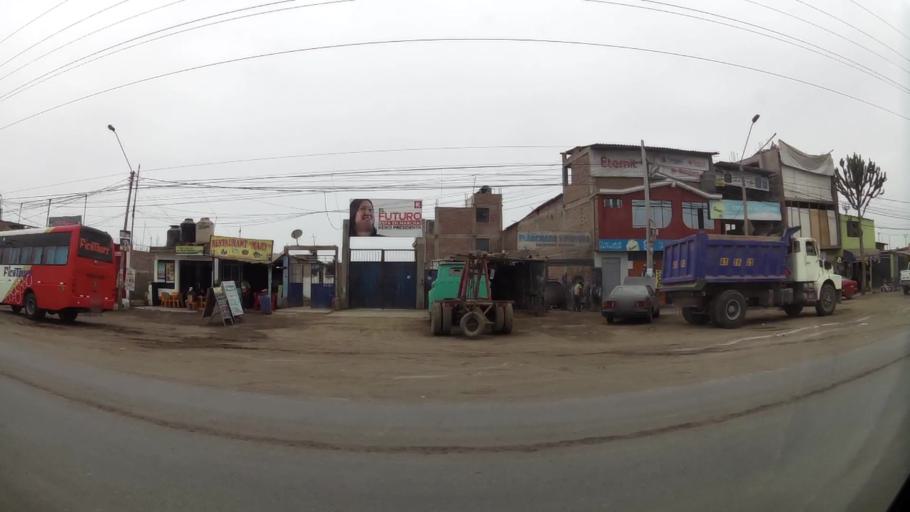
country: PE
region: Lima
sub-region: Lima
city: Punta Hermosa
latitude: -12.2618
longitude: -76.8831
